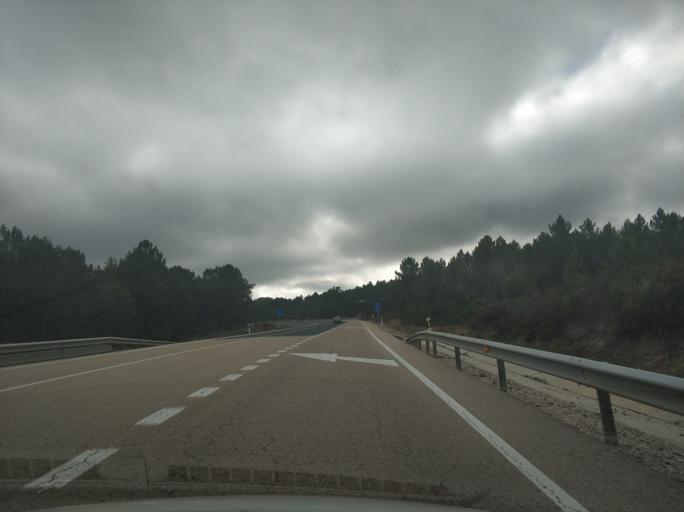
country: ES
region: Castille and Leon
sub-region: Provincia de Soria
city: Muriel Viejo
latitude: 41.8265
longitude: -2.9454
